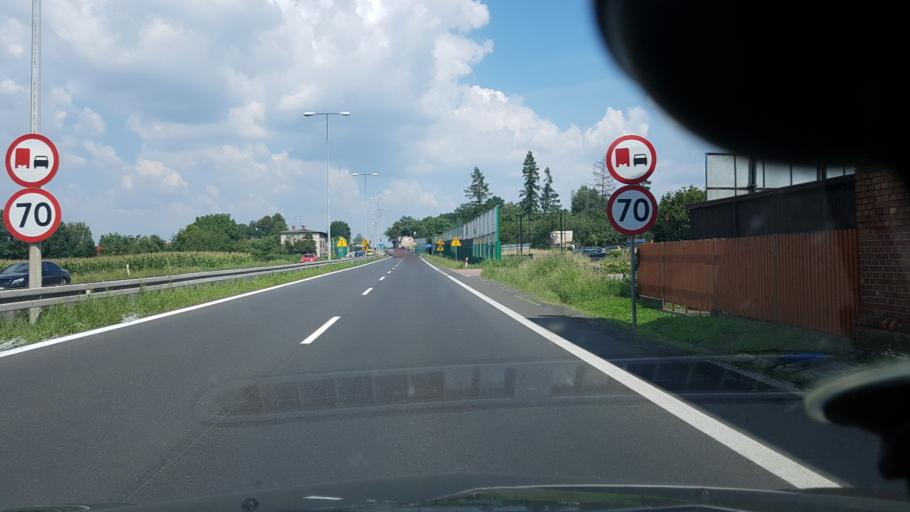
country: PL
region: Silesian Voivodeship
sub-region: Powiat mikolowski
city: Mikolow
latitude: 50.1856
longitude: 18.9168
